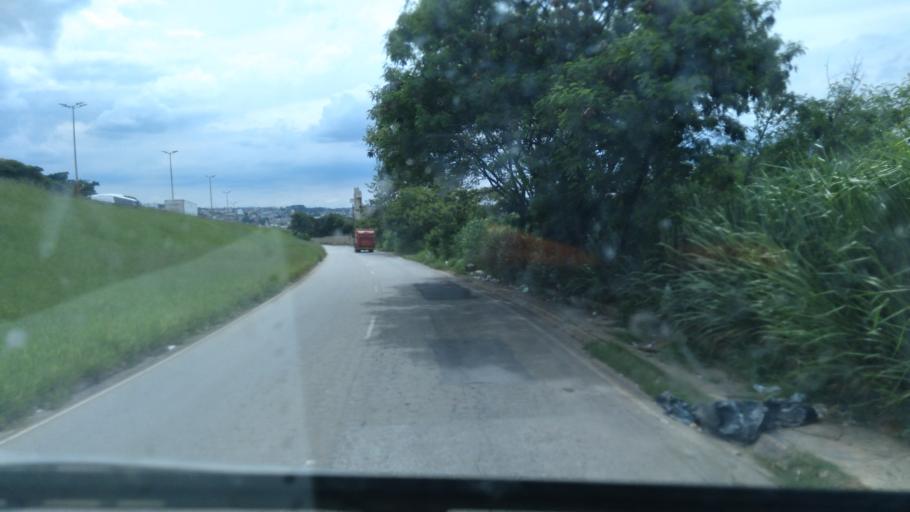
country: BR
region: Minas Gerais
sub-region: Belo Horizonte
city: Belo Horizonte
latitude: -19.8585
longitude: -43.9149
